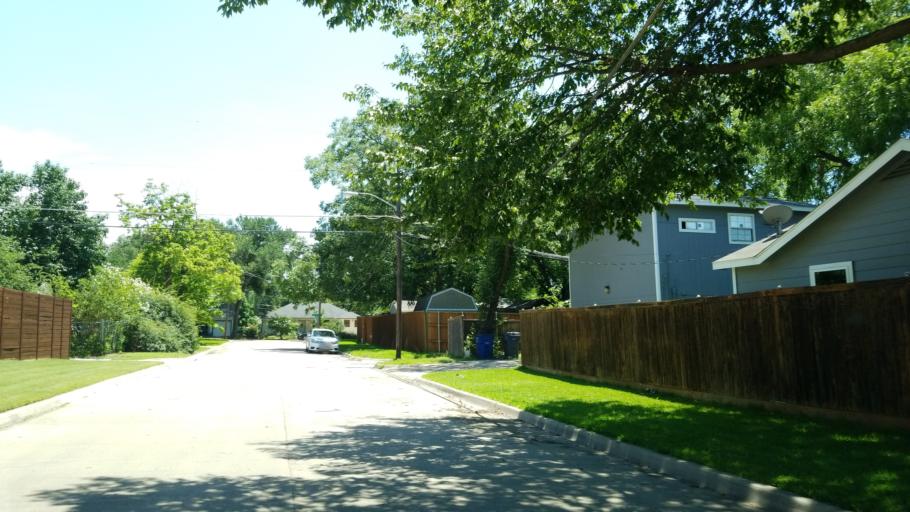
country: US
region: Texas
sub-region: Dallas County
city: University Park
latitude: 32.8770
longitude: -96.8503
